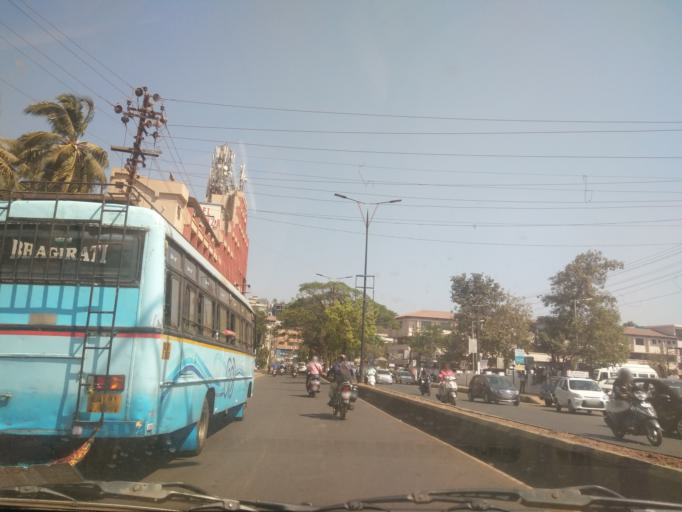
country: IN
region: Goa
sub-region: North Goa
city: Mapuca
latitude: 15.5891
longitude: 73.8092
